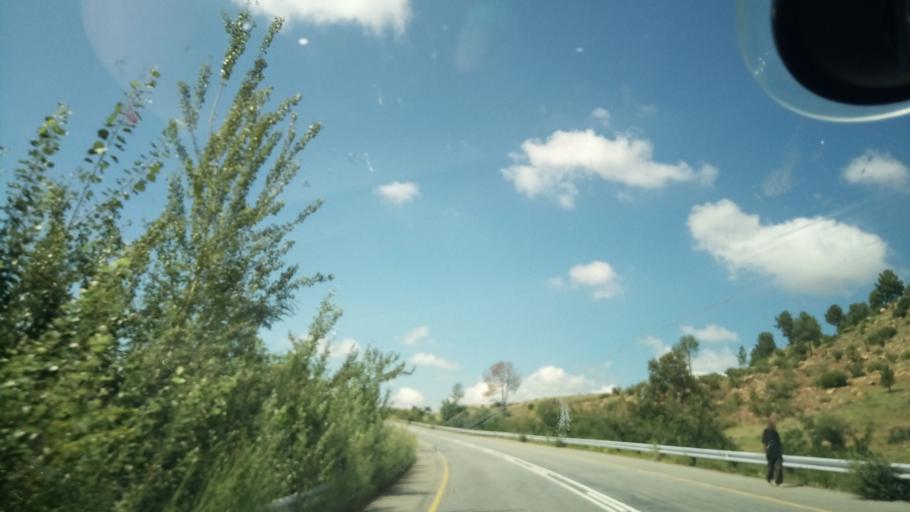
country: ZA
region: Orange Free State
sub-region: Thabo Mofutsanyana District Municipality
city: Ficksburg
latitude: -28.8793
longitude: 27.8655
